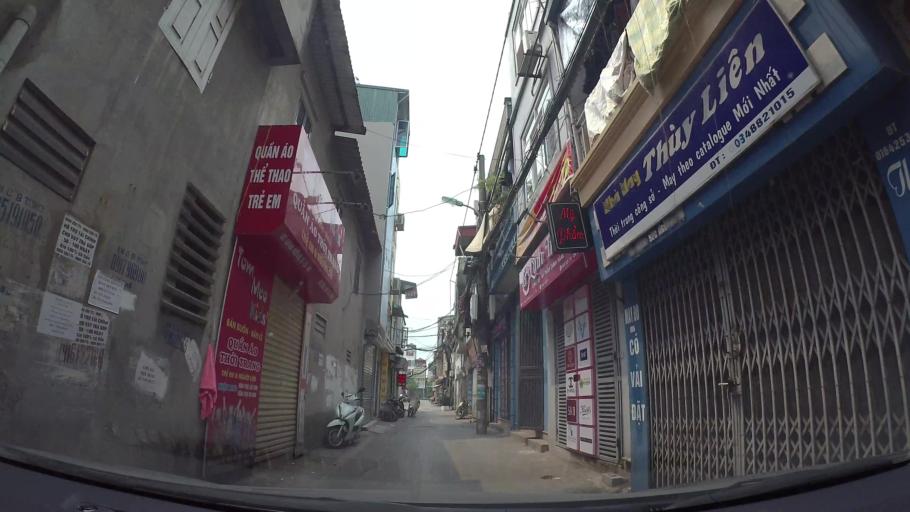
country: VN
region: Ha Noi
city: Trau Quy
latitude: 21.0710
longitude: 105.9051
